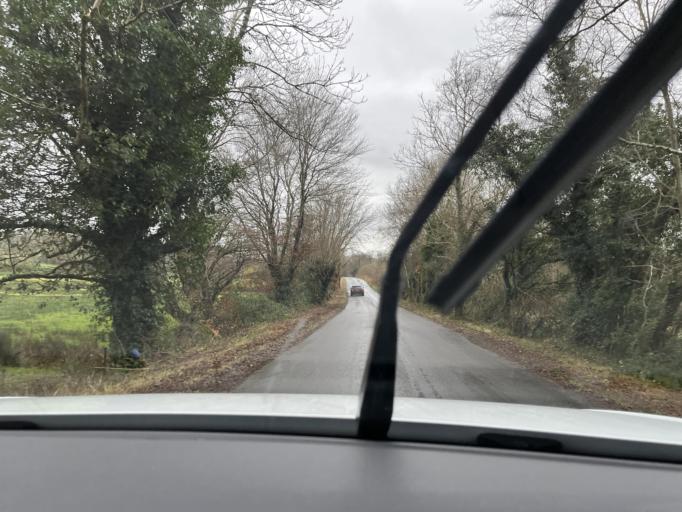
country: IE
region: Connaught
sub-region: County Leitrim
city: Manorhamilton
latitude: 54.2731
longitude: -8.2129
